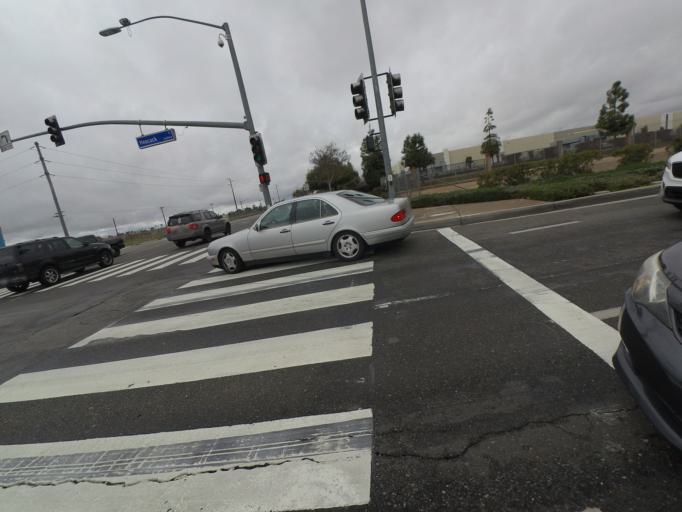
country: US
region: California
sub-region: Riverside County
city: March Air Force Base
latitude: 33.9103
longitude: -117.2436
